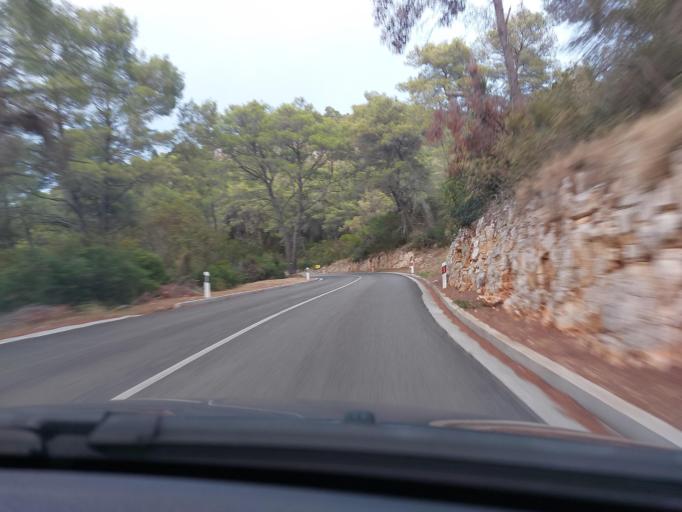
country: HR
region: Dubrovacko-Neretvanska
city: Smokvica
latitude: 42.7602
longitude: 16.8520
